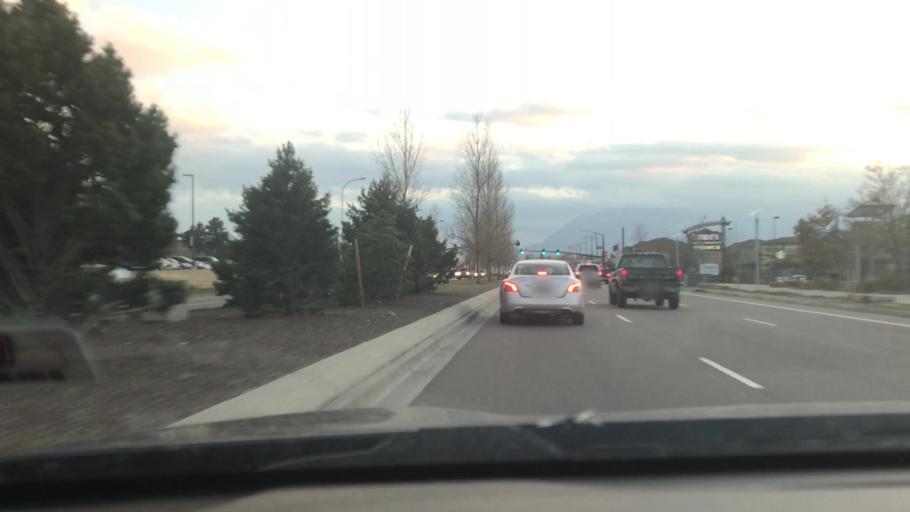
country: US
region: Colorado
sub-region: El Paso County
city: Colorado Springs
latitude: 38.9025
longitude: -104.8175
